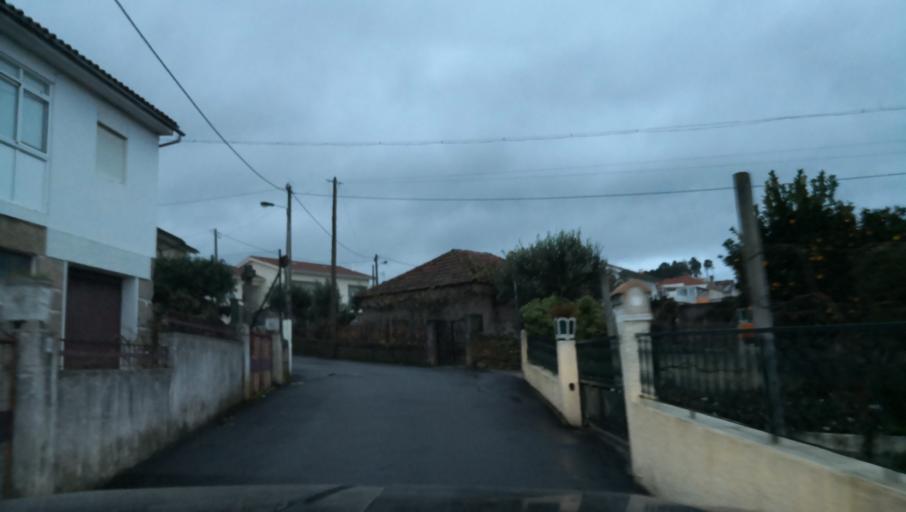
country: PT
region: Vila Real
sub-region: Vila Real
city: Vila Real
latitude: 41.2587
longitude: -7.7361
